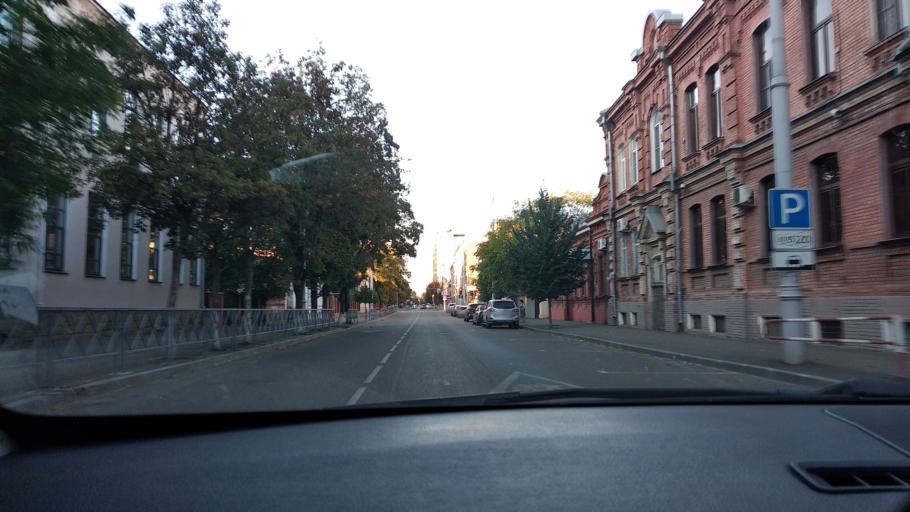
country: RU
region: Krasnodarskiy
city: Krasnodar
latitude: 45.0177
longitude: 38.9704
